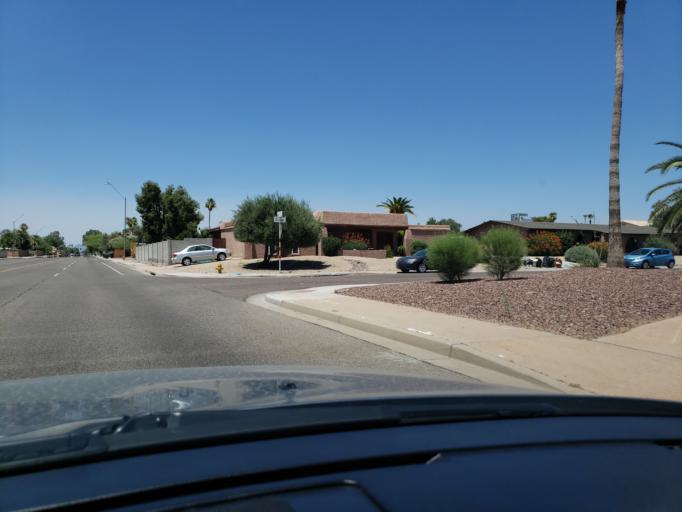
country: US
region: Arizona
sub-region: Maricopa County
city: Paradise Valley
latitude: 33.6061
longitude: -111.9433
